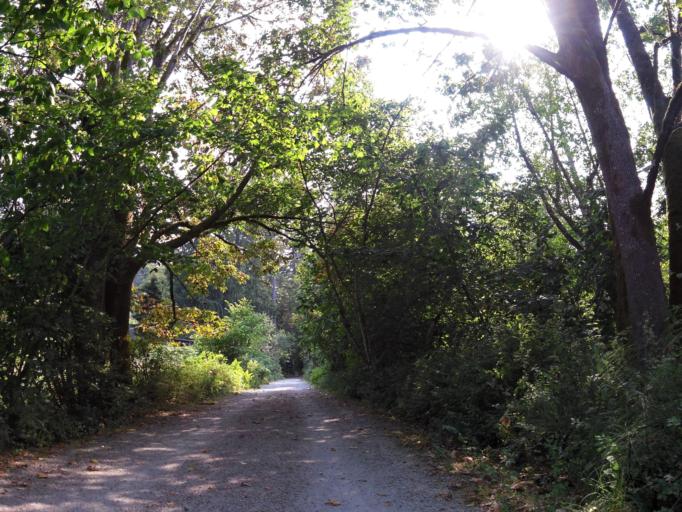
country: US
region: Washington
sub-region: Whatcom County
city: Bellingham
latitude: 48.7080
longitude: -122.4857
